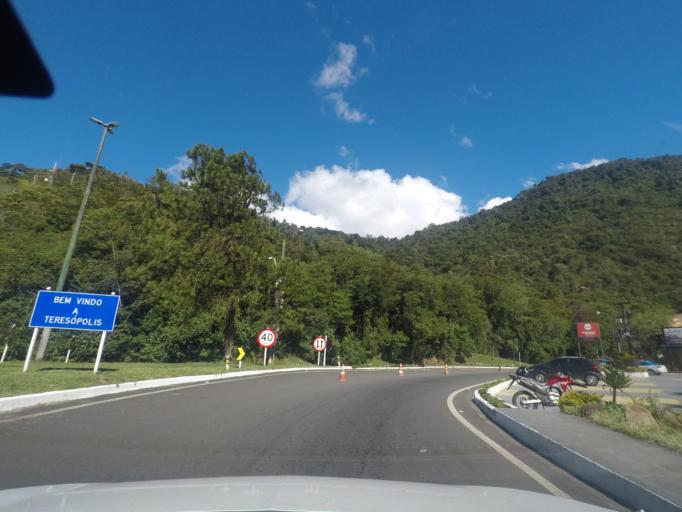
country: BR
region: Rio de Janeiro
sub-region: Teresopolis
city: Teresopolis
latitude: -22.4622
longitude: -42.9876
